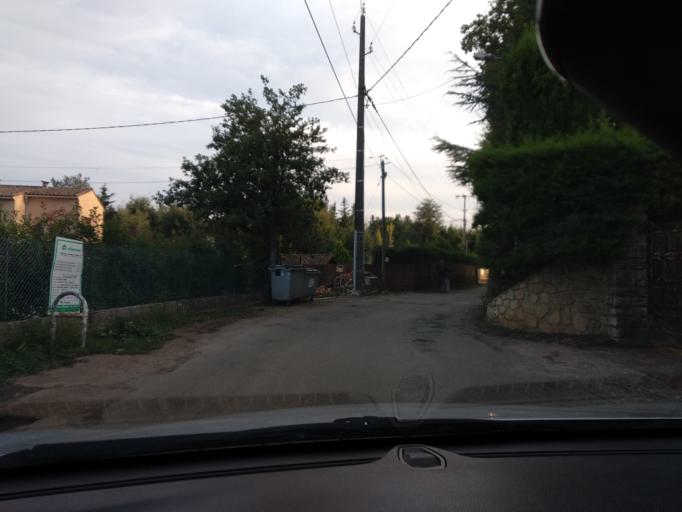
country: FR
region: Provence-Alpes-Cote d'Azur
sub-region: Departement des Alpes-Maritimes
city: Saint-Cezaire-sur-Siagne
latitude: 43.6550
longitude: 6.8015
